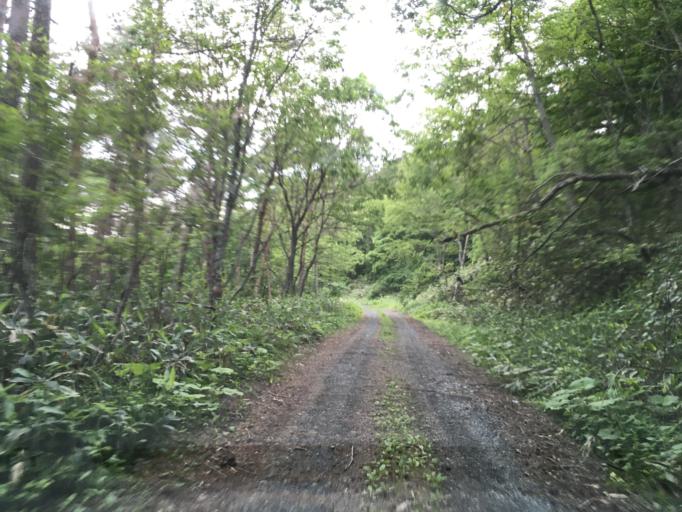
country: JP
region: Iwate
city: Mizusawa
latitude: 39.1306
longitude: 141.3246
